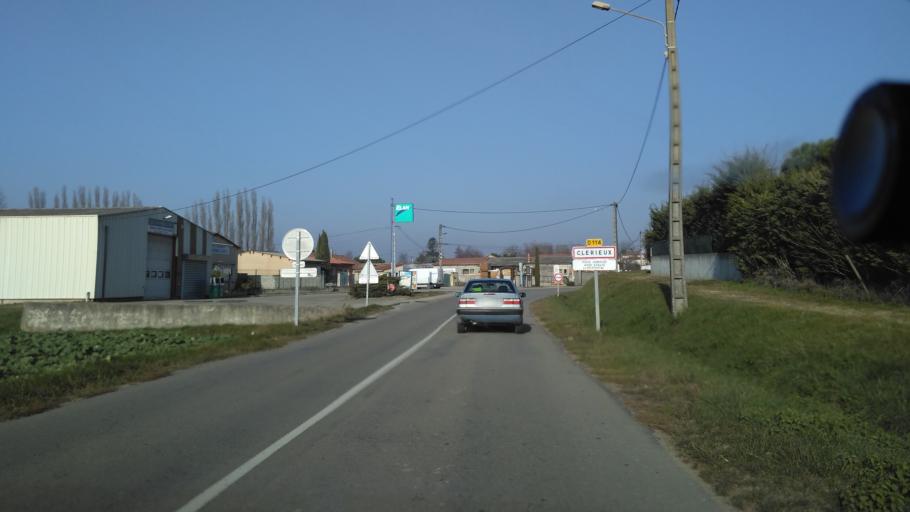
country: FR
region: Rhone-Alpes
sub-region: Departement de la Drome
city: Clerieux
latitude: 45.0717
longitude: 4.9586
